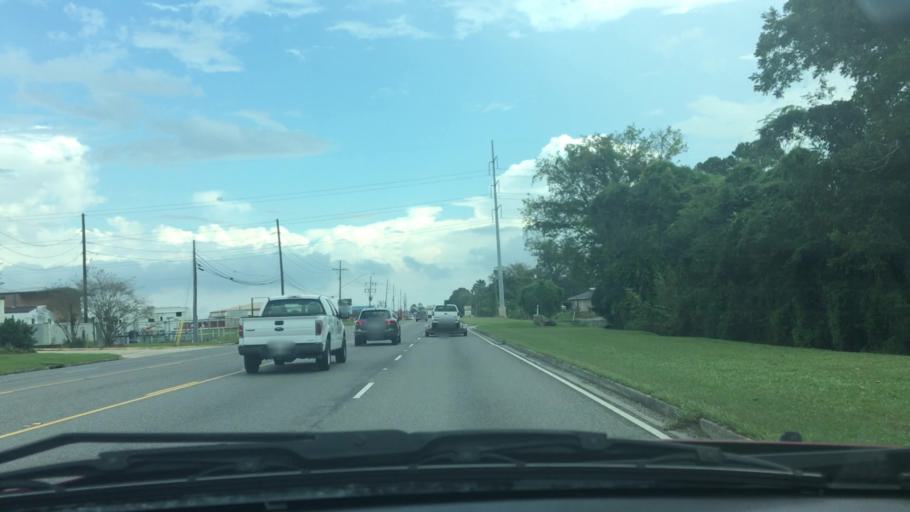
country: US
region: Louisiana
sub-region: Saint John the Baptist Parish
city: Laplace
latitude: 30.0684
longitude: -90.4798
